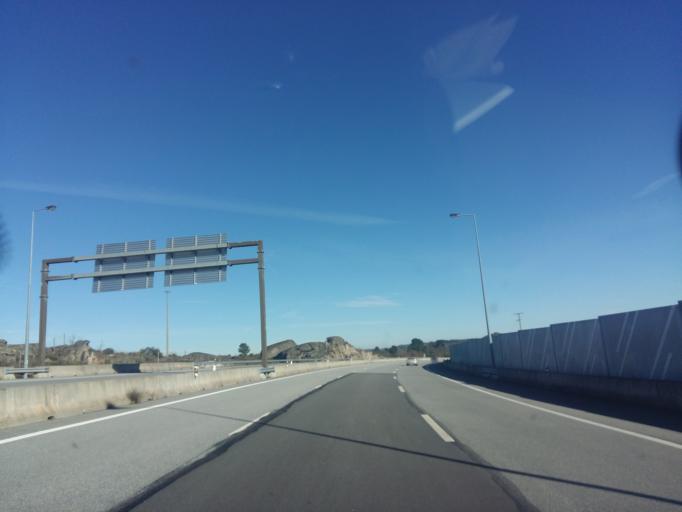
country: PT
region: Guarda
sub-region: Guarda
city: Sequeira
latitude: 40.5717
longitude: -7.2107
